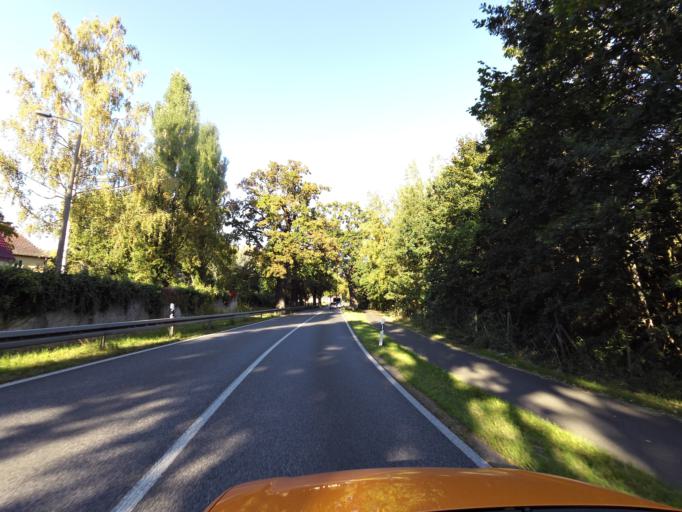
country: DE
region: Brandenburg
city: Potsdam
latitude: 52.4567
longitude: 13.0478
